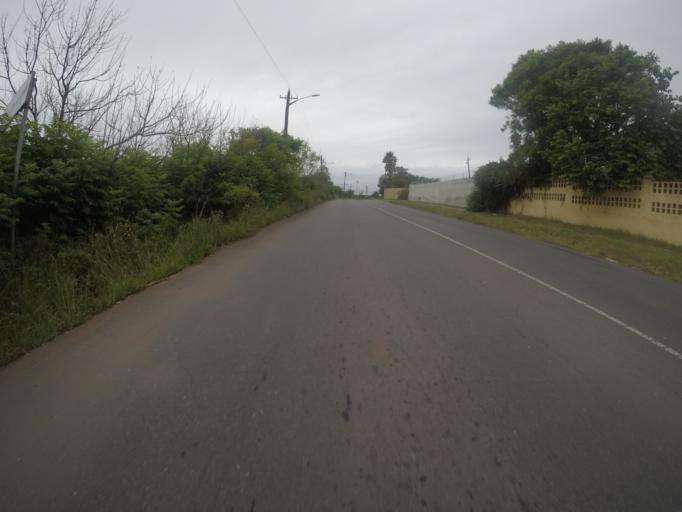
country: ZA
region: Eastern Cape
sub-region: Buffalo City Metropolitan Municipality
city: East London
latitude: -32.9719
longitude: 27.8809
